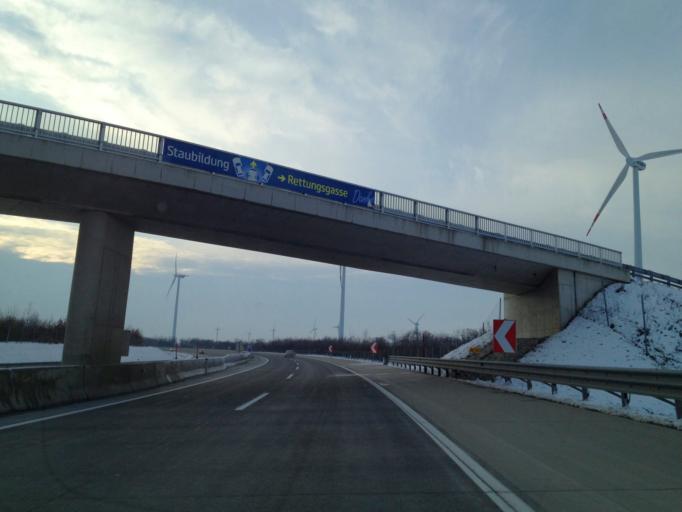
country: AT
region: Burgenland
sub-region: Politischer Bezirk Neusiedl am See
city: Potzneusiedl
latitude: 48.0402
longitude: 16.9012
